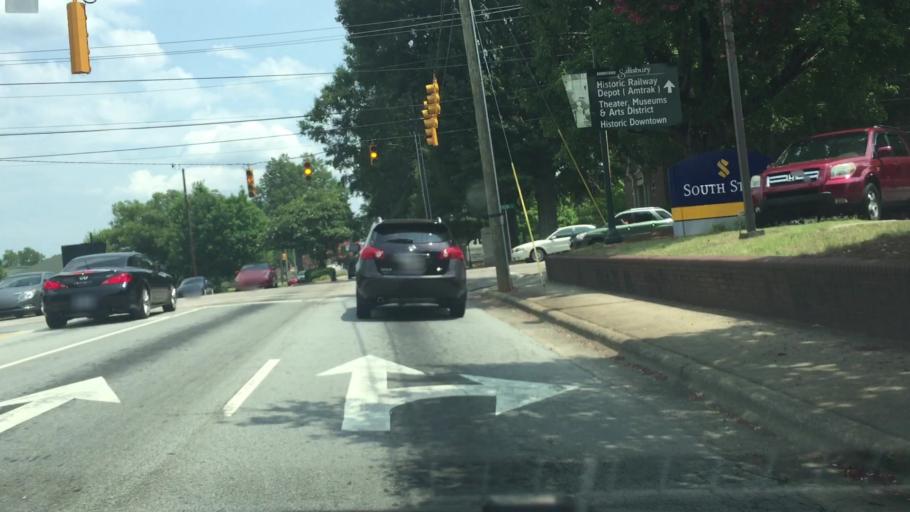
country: US
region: North Carolina
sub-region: Rowan County
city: Salisbury
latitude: 35.6702
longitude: -80.4734
